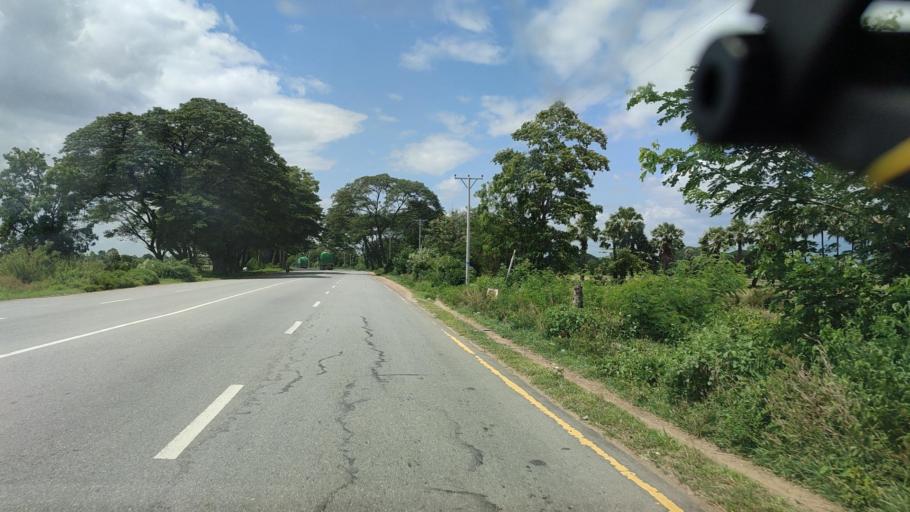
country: MM
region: Mandalay
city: Yamethin
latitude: 20.2273
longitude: 96.1793
